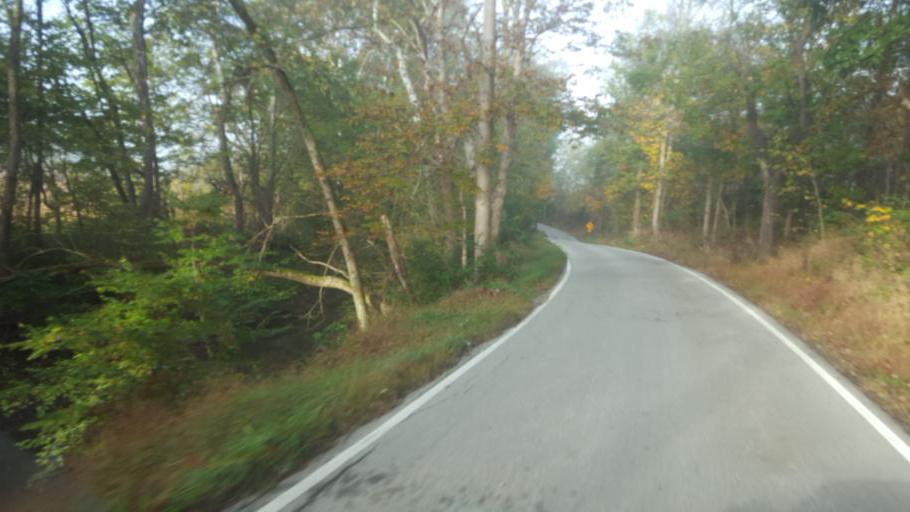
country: US
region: Kentucky
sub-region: Fleming County
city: Flemingsburg
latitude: 38.4908
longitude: -83.5916
